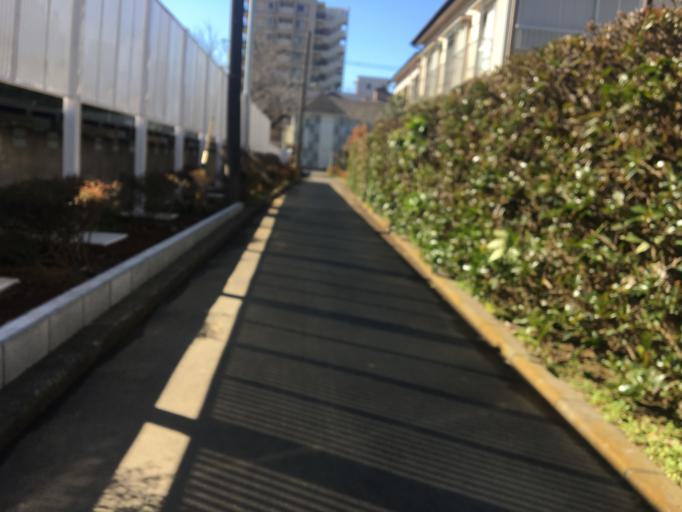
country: JP
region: Saitama
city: Shiki
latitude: 35.8074
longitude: 139.5683
